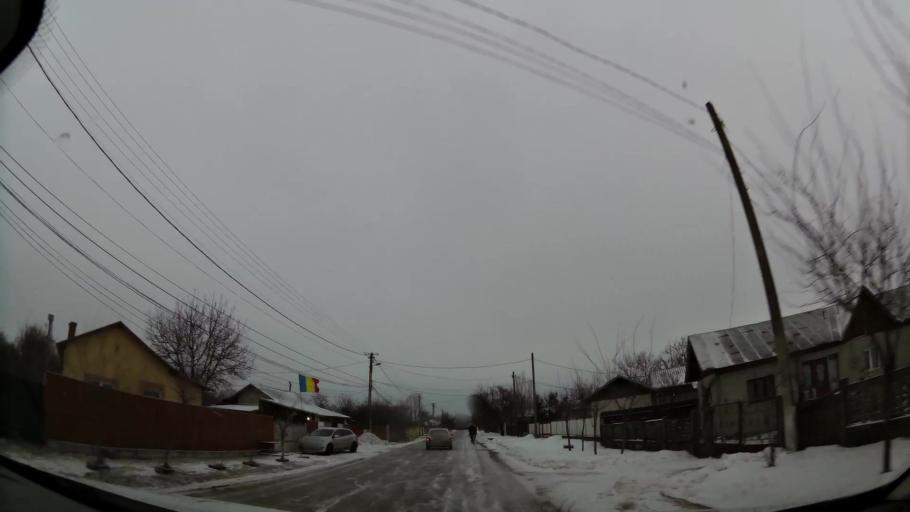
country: RO
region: Prahova
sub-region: Comuna Poenarii-Burchi
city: Ologeni
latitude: 44.7308
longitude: 25.9527
